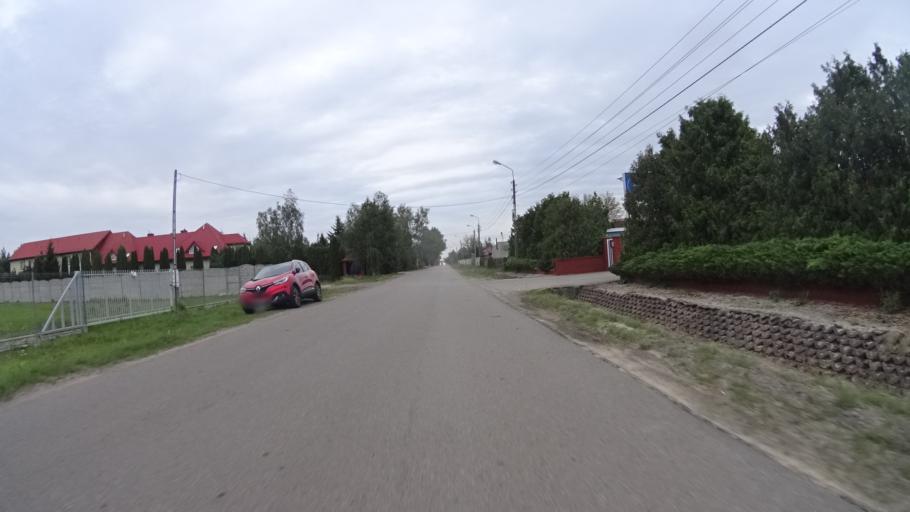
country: PL
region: Masovian Voivodeship
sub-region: Powiat warszawski zachodni
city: Ozarow Mazowiecki
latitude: 52.2474
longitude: 20.7878
